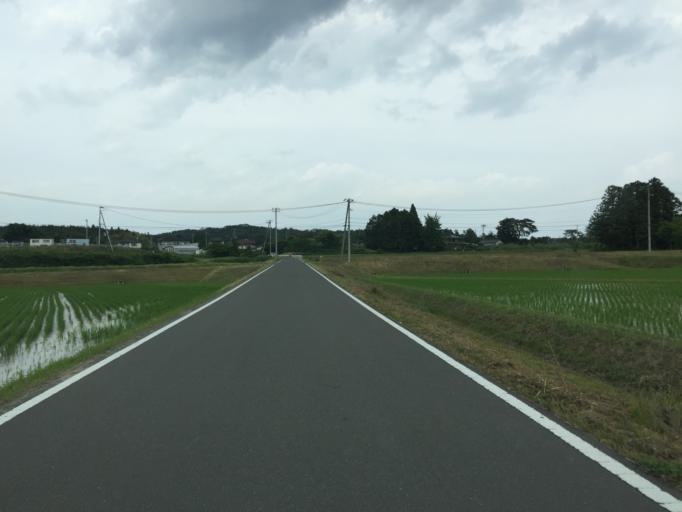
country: JP
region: Miyagi
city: Marumori
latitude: 37.7679
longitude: 140.9360
